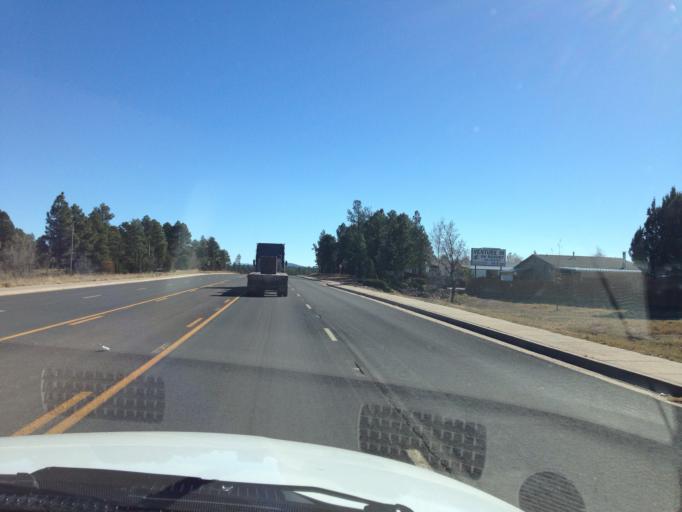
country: US
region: Arizona
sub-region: Navajo County
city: Show Low
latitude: 34.2523
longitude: -110.0808
